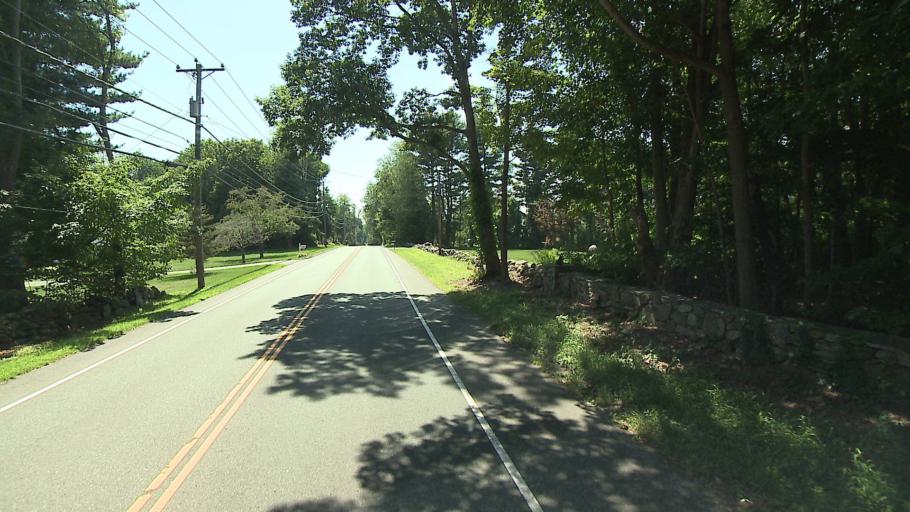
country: US
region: Connecticut
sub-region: Fairfield County
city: Shelton
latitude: 41.3552
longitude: -73.1971
